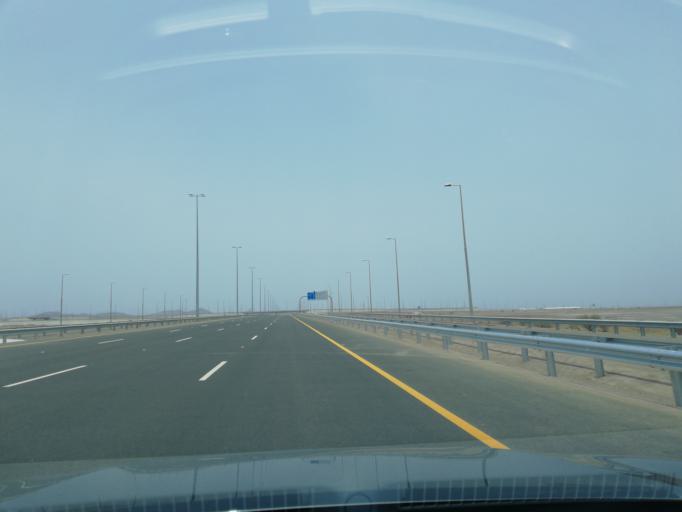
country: OM
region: Al Batinah
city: Al Liwa'
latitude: 24.4475
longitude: 56.5191
